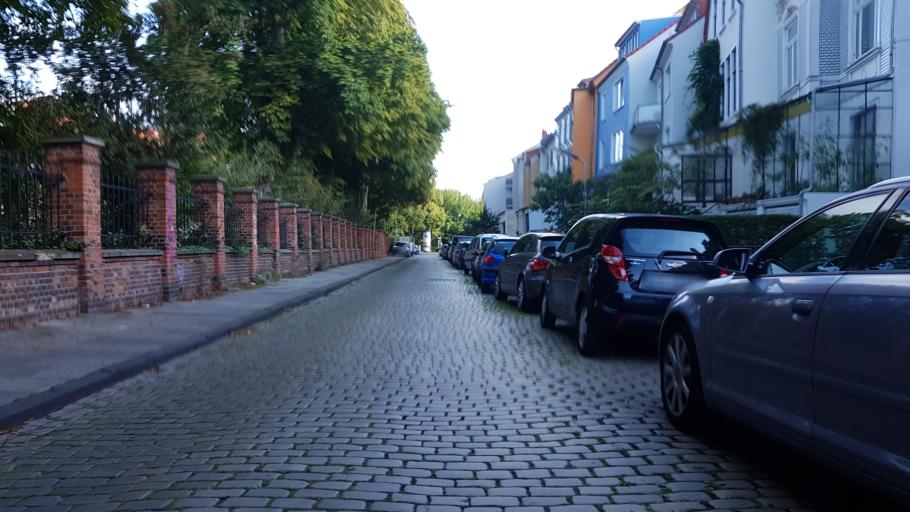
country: DE
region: Bremen
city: Bremen
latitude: 53.0696
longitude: 8.7947
